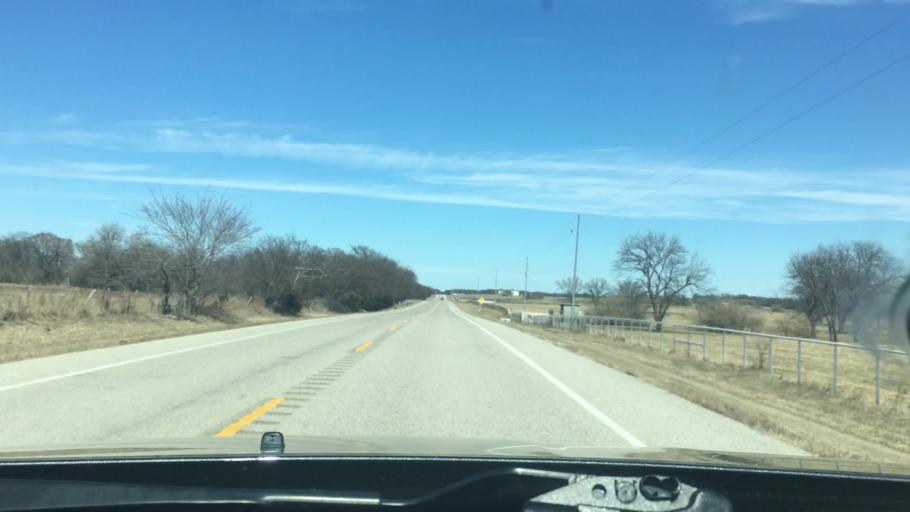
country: US
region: Oklahoma
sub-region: Murray County
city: Sulphur
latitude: 34.3691
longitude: -96.9508
